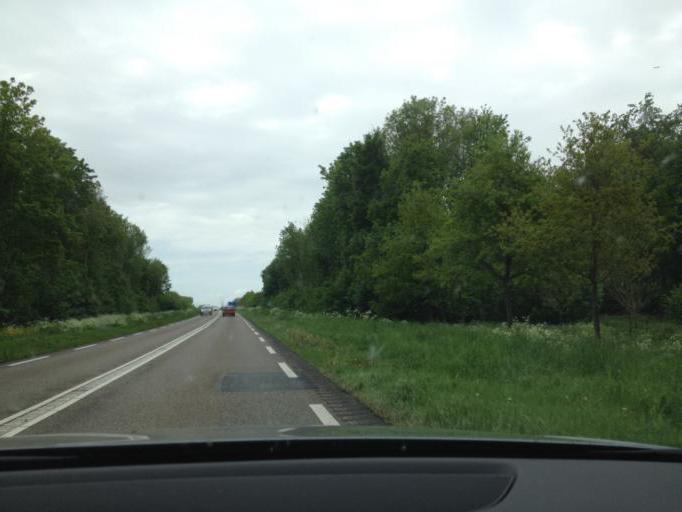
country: NL
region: Flevoland
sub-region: Gemeente Almere
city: Almere Stad
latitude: 52.3483
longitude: 5.2611
